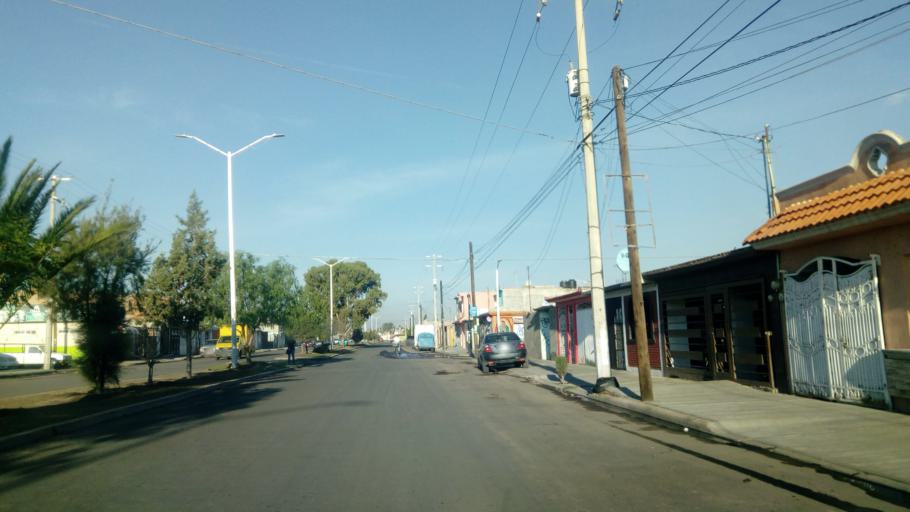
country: MX
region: Durango
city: Victoria de Durango
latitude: 24.0539
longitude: -104.5980
